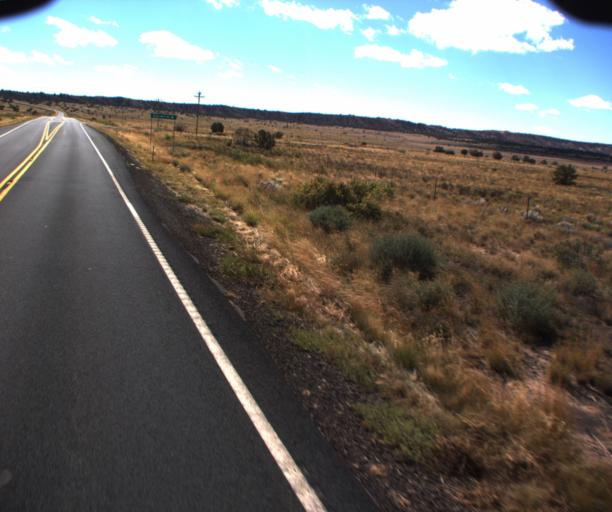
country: US
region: Arizona
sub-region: Apache County
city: Houck
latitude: 35.0482
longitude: -109.2732
